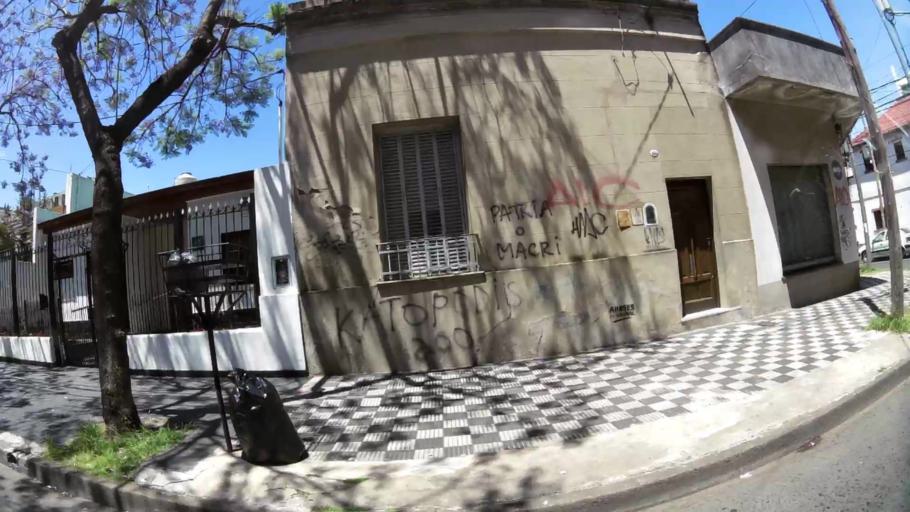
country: AR
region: Buenos Aires
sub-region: Partido de General San Martin
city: General San Martin
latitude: -34.5815
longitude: -58.5378
